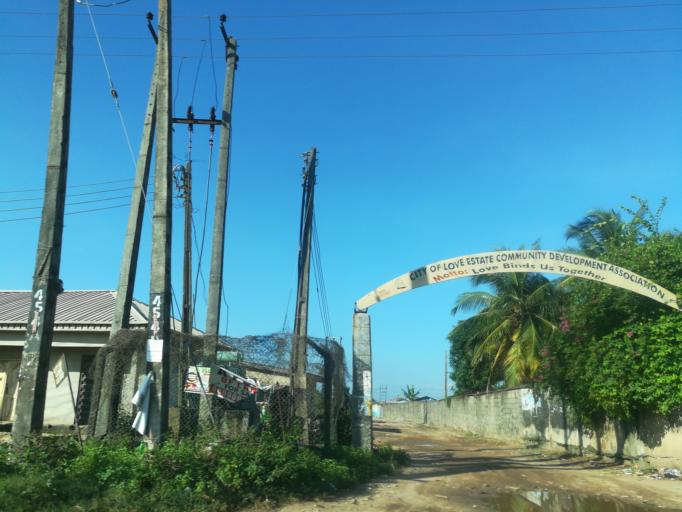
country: NG
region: Lagos
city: Ebute Ikorodu
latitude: 6.5405
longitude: 3.5490
